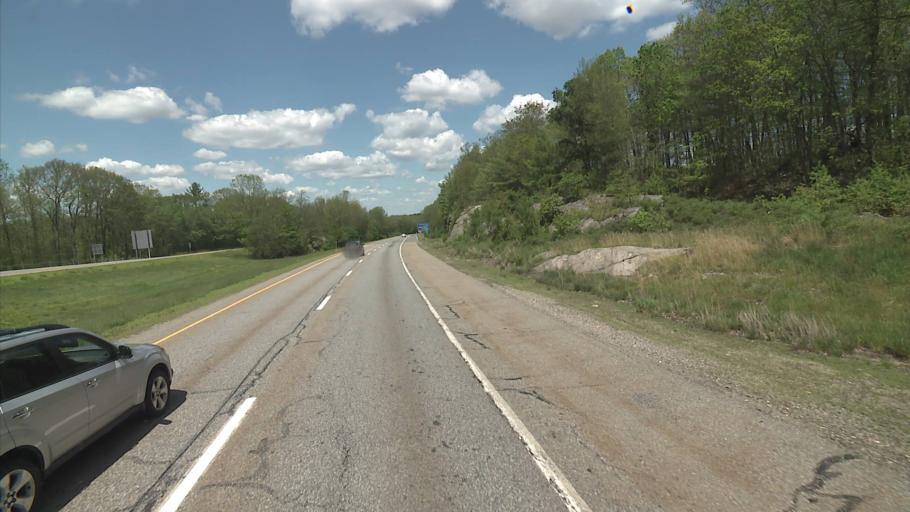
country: US
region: Massachusetts
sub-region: Worcester County
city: Webster
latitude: 42.0232
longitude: -71.8603
